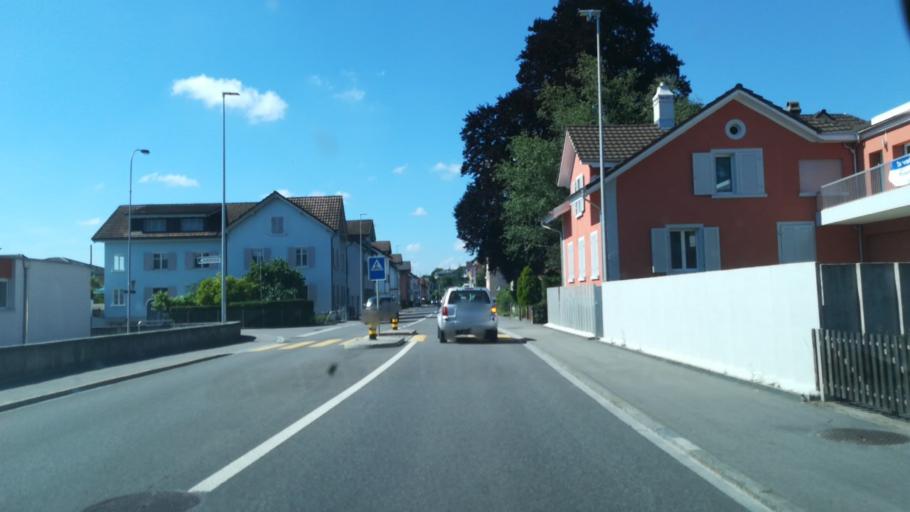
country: CH
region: Thurgau
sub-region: Weinfelden District
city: Sulgen
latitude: 47.5352
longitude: 9.1867
